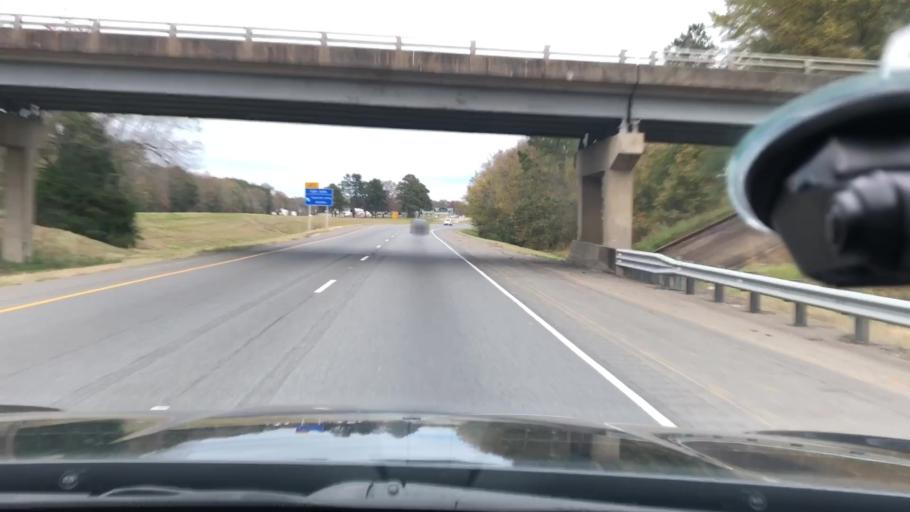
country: US
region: Arkansas
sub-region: Hot Spring County
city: Malvern
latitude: 34.3480
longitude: -92.8959
